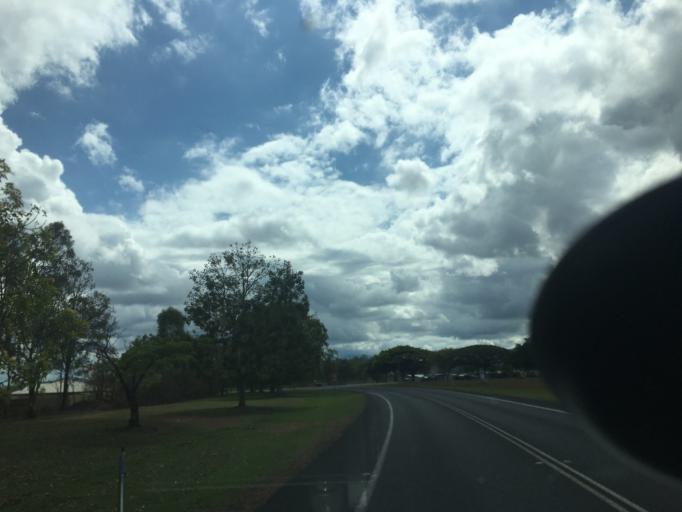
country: AU
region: Queensland
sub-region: Tablelands
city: Mareeba
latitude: -17.0109
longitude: 145.4293
